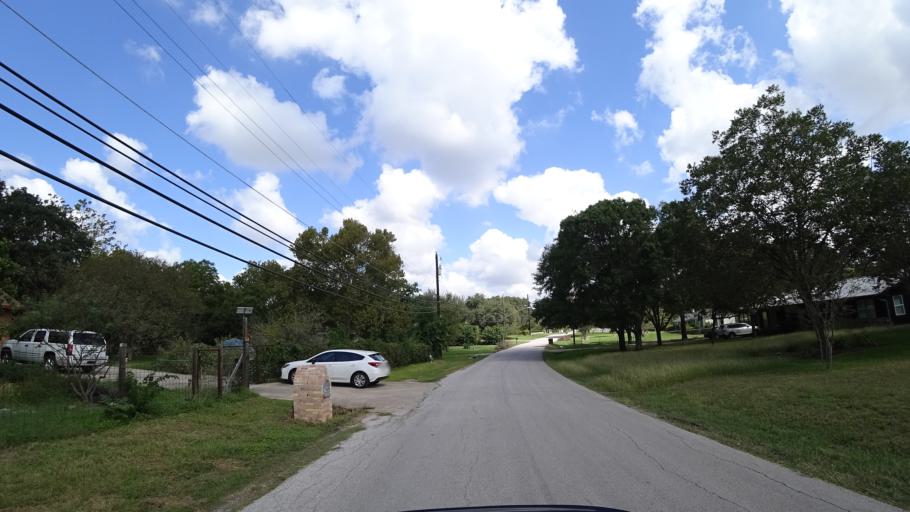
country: US
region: Texas
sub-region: Travis County
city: Onion Creek
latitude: 30.1937
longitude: -97.8004
